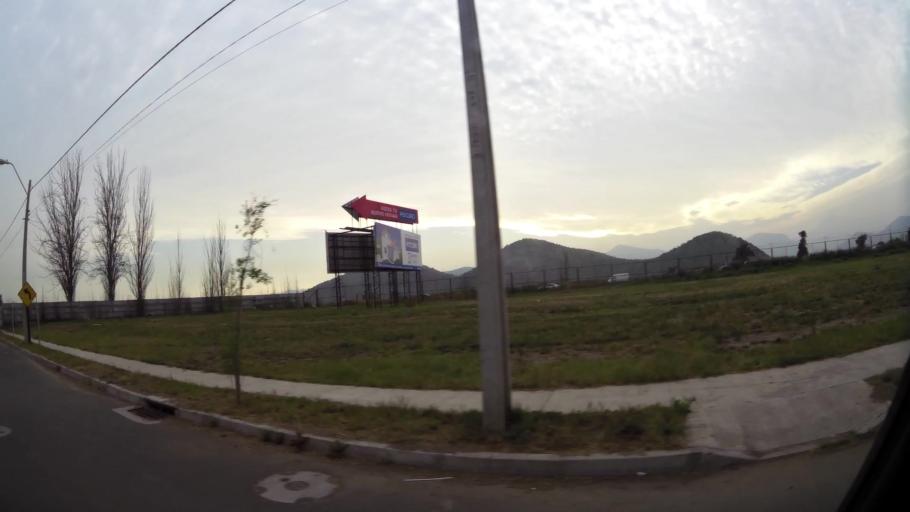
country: CL
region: Santiago Metropolitan
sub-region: Provincia de Talagante
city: Penaflor
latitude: -33.5338
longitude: -70.8001
